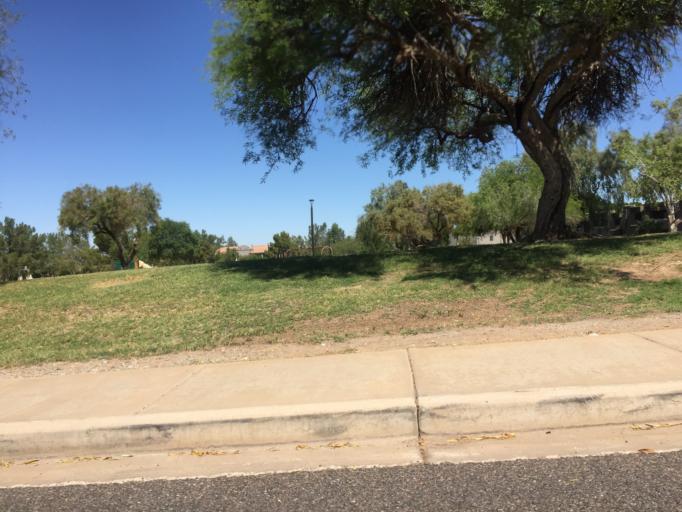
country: US
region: Arizona
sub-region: Maricopa County
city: Paradise Valley
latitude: 33.5436
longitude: -112.0416
